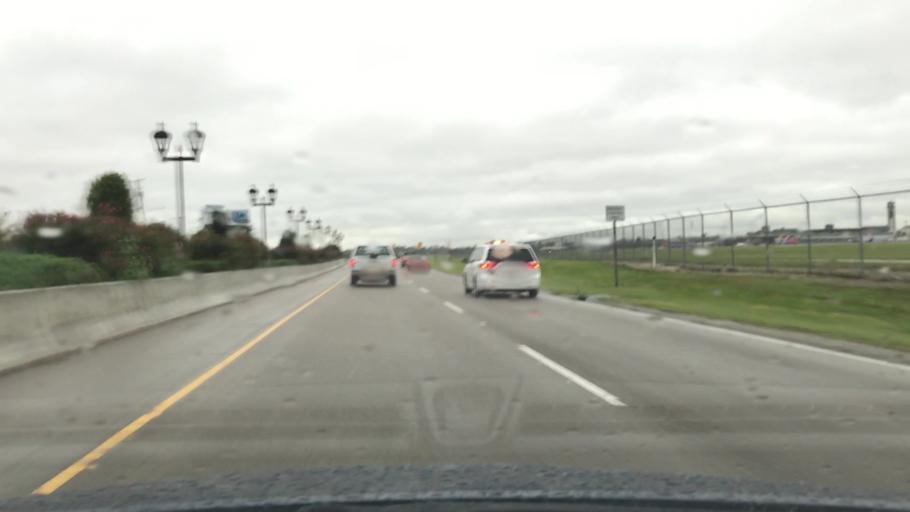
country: US
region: Louisiana
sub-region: Jefferson Parish
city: Kenner
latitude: 29.9926
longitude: -90.2474
